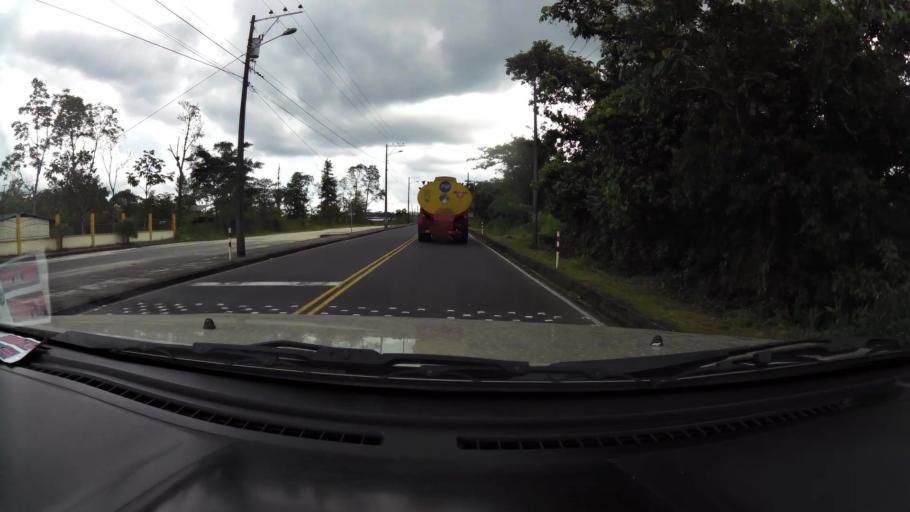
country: EC
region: Pastaza
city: Puyo
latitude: -1.4538
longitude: -78.1222
